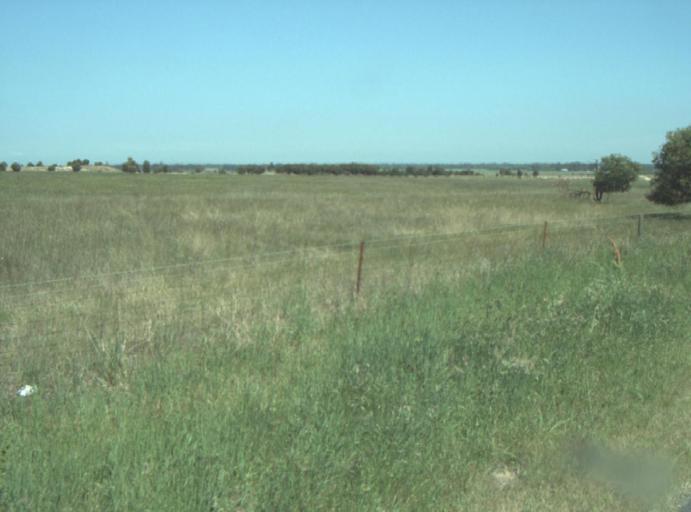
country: AU
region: Victoria
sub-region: Greater Geelong
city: Lara
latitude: -37.9673
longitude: 144.4063
